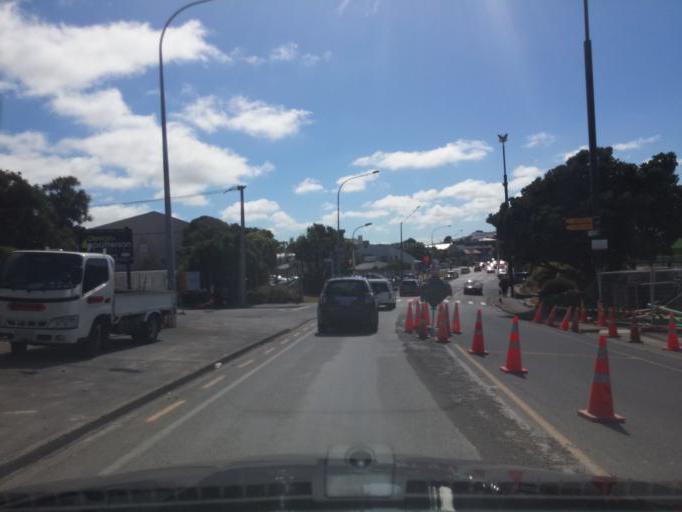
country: NZ
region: Wellington
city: Petone
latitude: -41.2234
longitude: 174.8044
